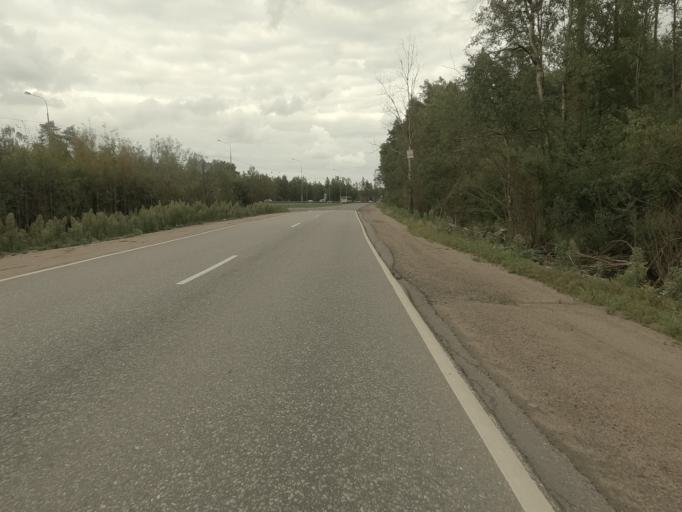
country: RU
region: Leningrad
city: Shcheglovo
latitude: 59.9033
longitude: 30.7766
